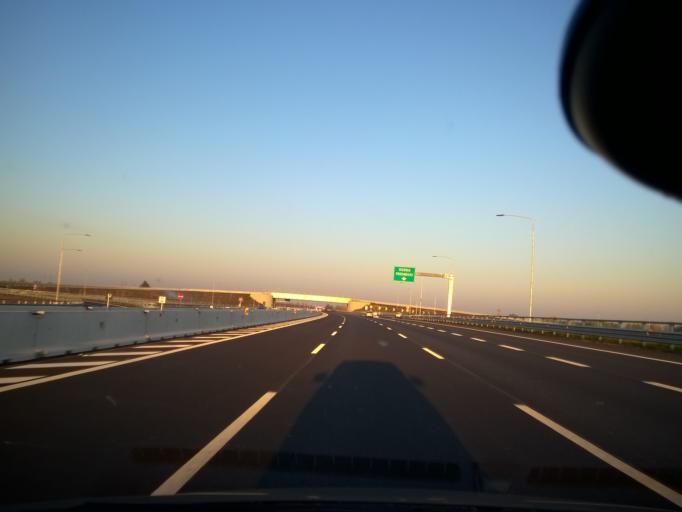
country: IT
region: Lombardy
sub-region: Citta metropolitana di Milano
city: Vizzolo Predabissi
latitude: 45.3495
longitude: 9.3501
